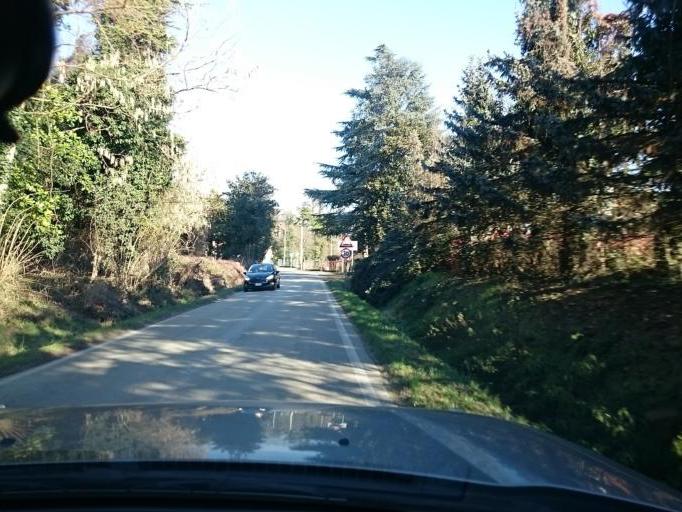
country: IT
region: Veneto
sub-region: Provincia di Padova
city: Saonara
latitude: 45.3710
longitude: 11.9780
